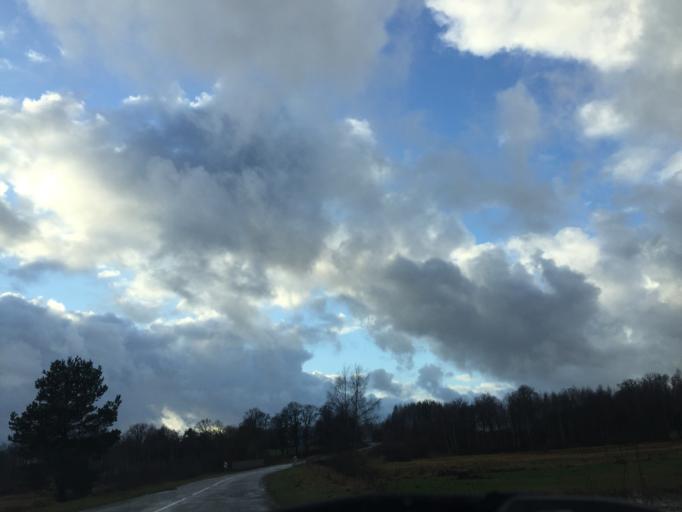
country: LV
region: Burtnieki
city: Matisi
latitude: 57.6840
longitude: 25.2960
